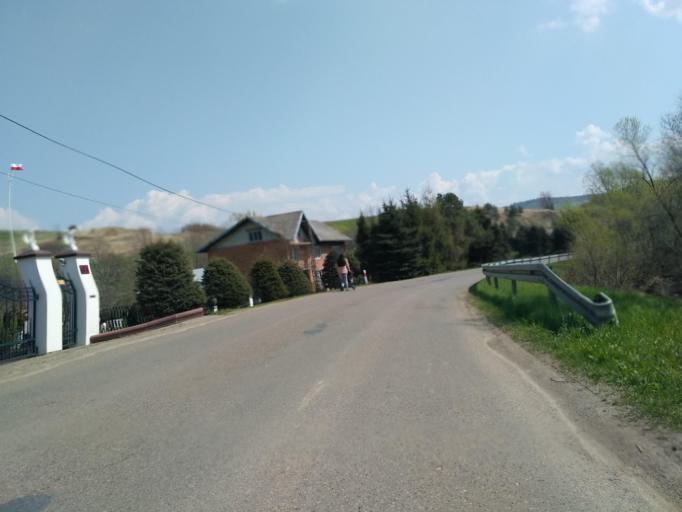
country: PL
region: Subcarpathian Voivodeship
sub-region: Powiat sanocki
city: Bukowsko
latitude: 49.5154
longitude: 22.0221
